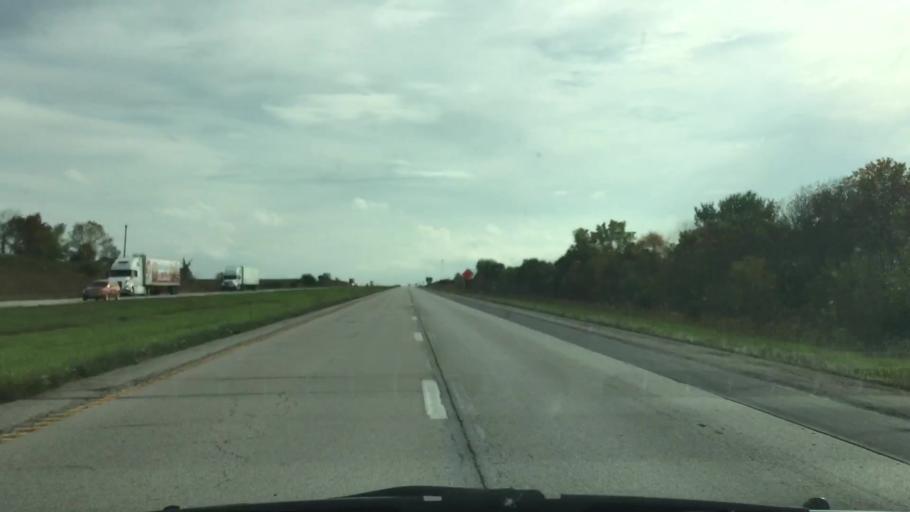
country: US
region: Iowa
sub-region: Decatur County
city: Lamoni
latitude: 40.5314
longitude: -93.9587
